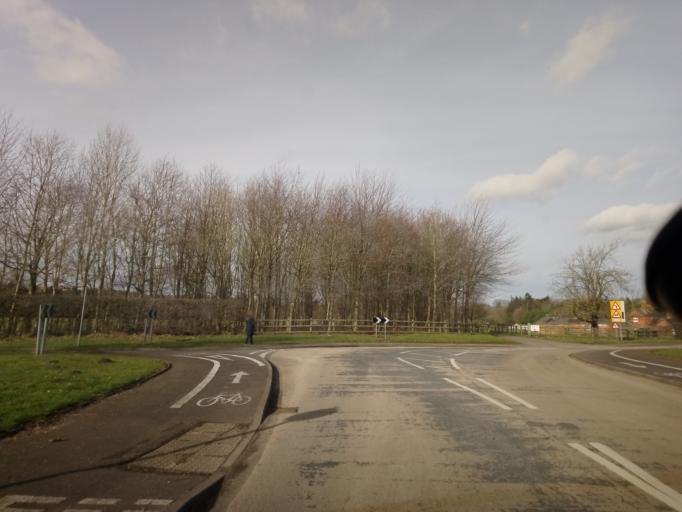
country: GB
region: England
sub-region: Shropshire
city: Stoke upon Tern
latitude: 52.8469
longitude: -2.5741
